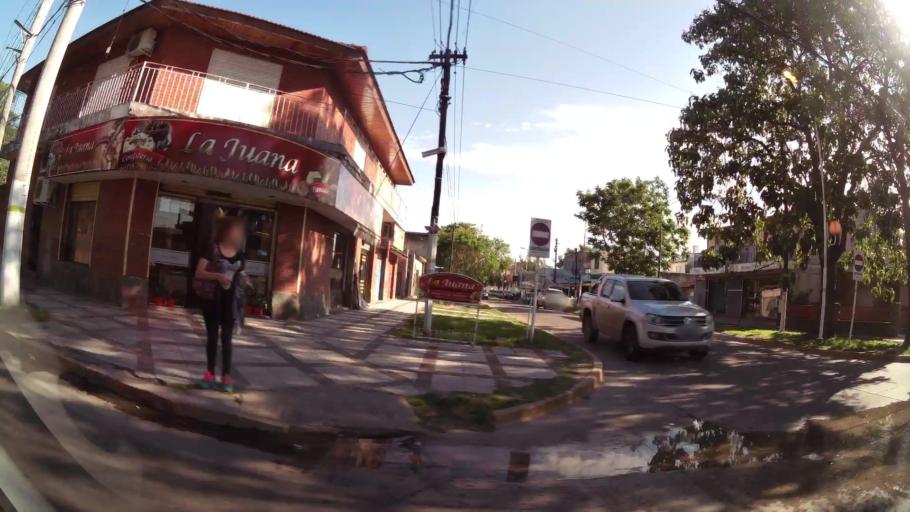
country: AR
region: Buenos Aires
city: Santa Catalina - Dique Lujan
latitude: -34.4928
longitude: -58.7053
